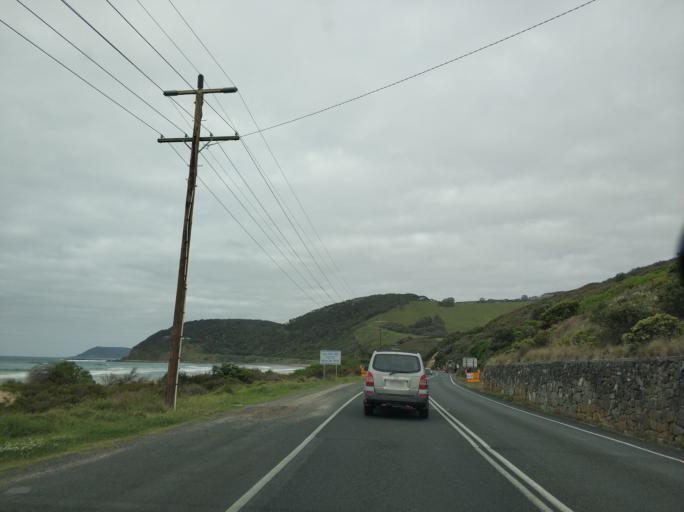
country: AU
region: Victoria
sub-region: Surf Coast
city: Anglesea
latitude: -38.4729
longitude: 144.0419
